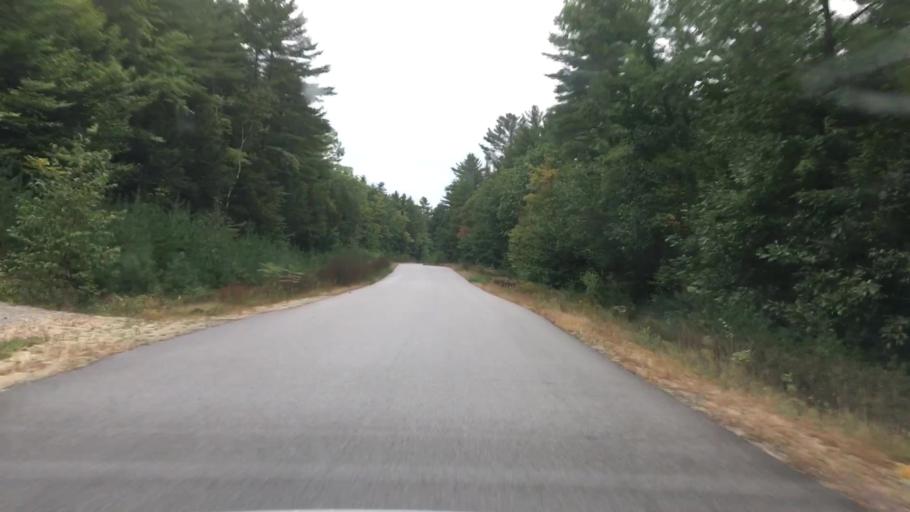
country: US
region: Maine
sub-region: Cumberland County
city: Harrison
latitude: 44.0256
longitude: -70.5909
